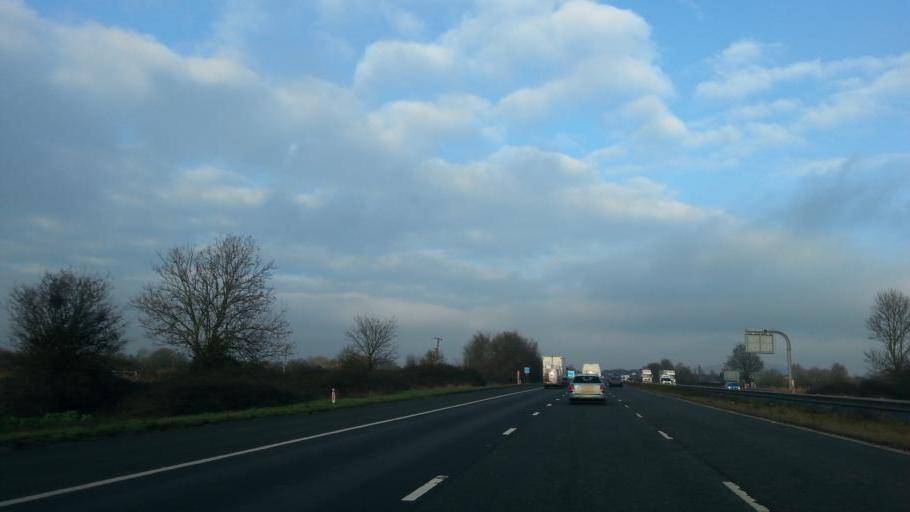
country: GB
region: England
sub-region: Gloucestershire
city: Stonehouse
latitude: 51.7905
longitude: -2.2973
